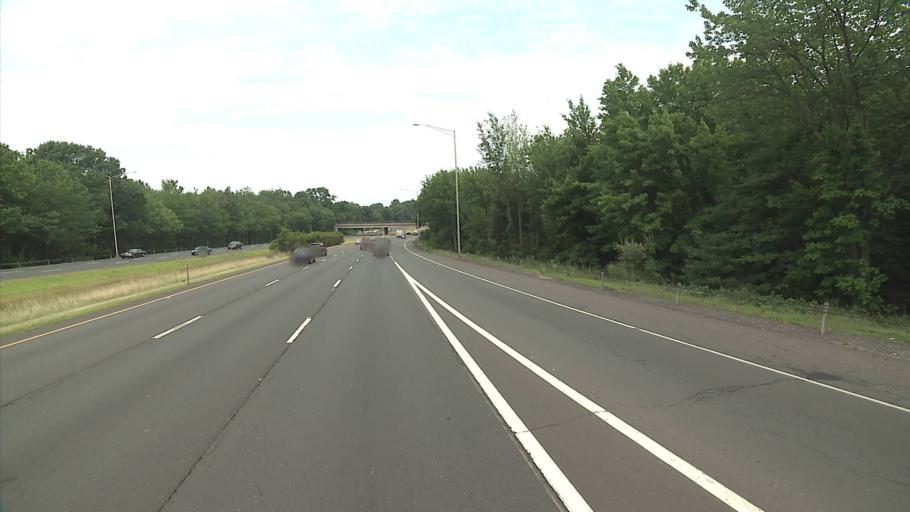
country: US
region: Connecticut
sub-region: New Haven County
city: Wolcott
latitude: 41.5894
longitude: -72.9011
